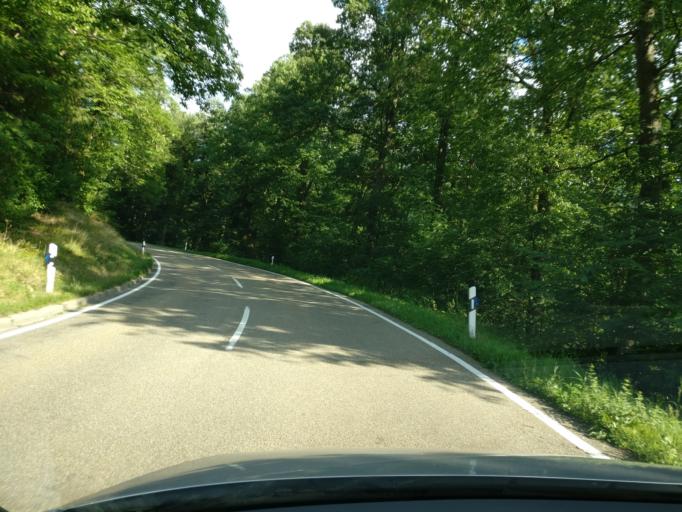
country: DE
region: Baden-Wuerttemberg
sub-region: Karlsruhe Region
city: Loffenau
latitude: 48.7745
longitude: 8.4014
